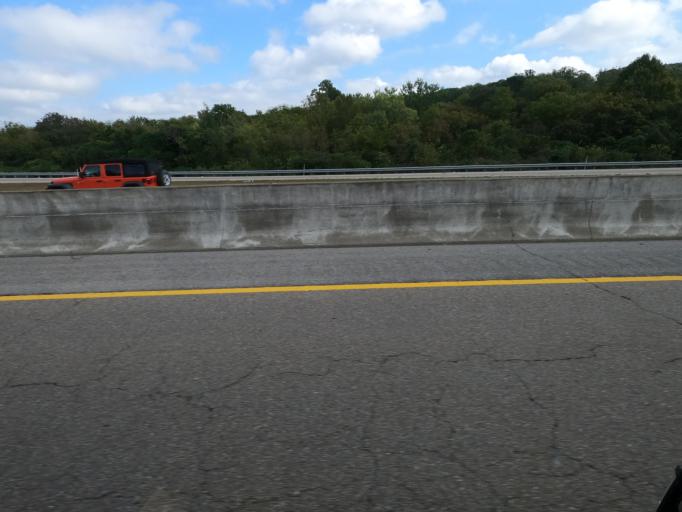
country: US
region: Tennessee
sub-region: Knox County
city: Farragut
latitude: 35.8991
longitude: -84.1172
